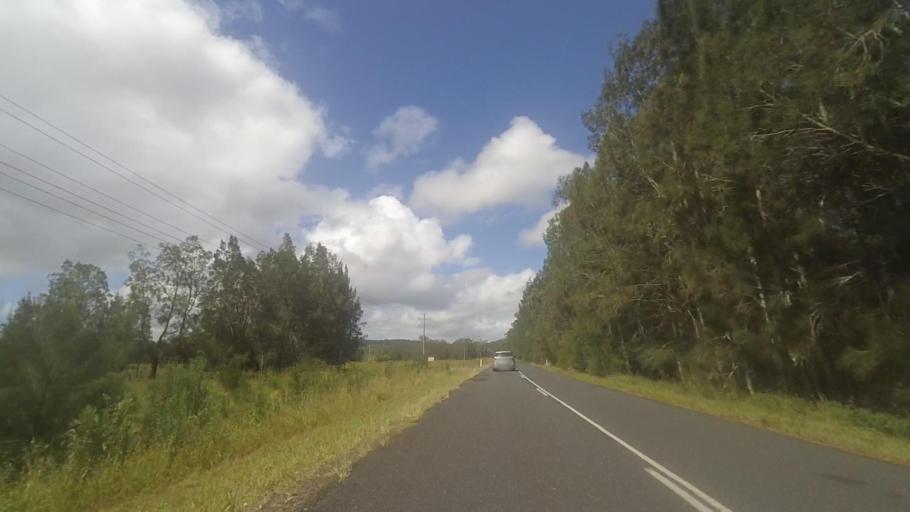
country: AU
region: New South Wales
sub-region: Great Lakes
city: Bulahdelah
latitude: -32.3909
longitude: 152.3288
